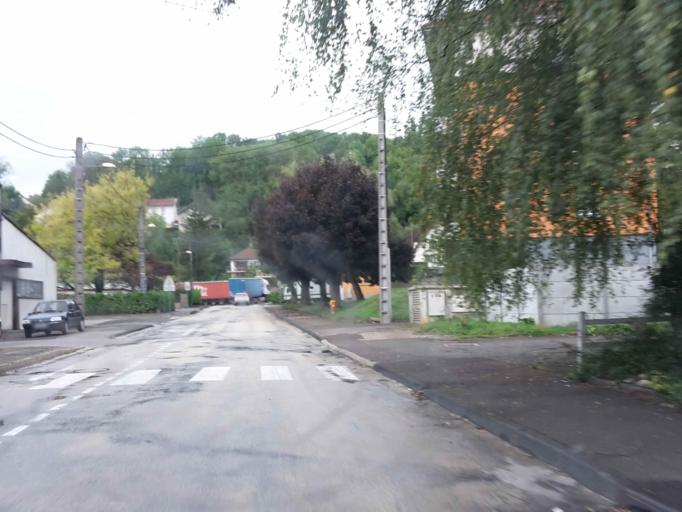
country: FR
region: Franche-Comte
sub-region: Departement du Doubs
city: Baume-les-Dames
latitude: 47.3497
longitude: 6.3683
